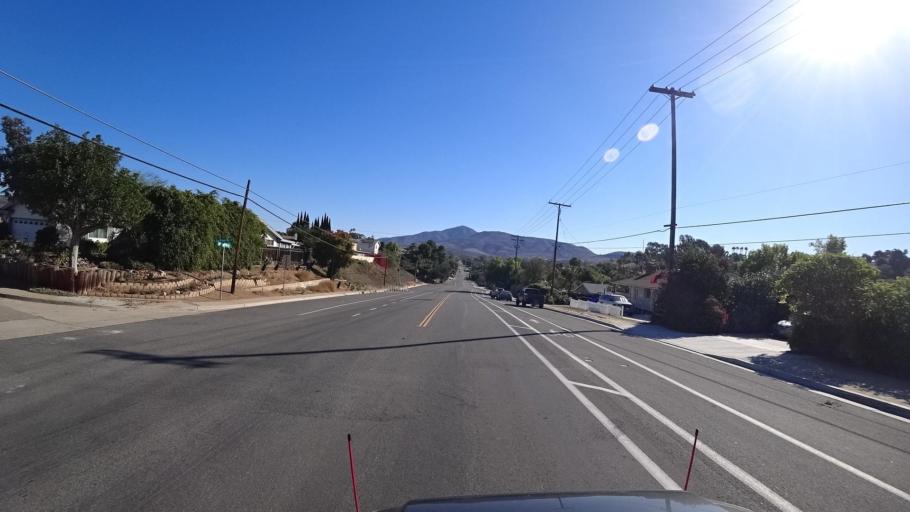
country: US
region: California
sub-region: San Diego County
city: Bonita
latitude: 32.6758
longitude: -117.0114
